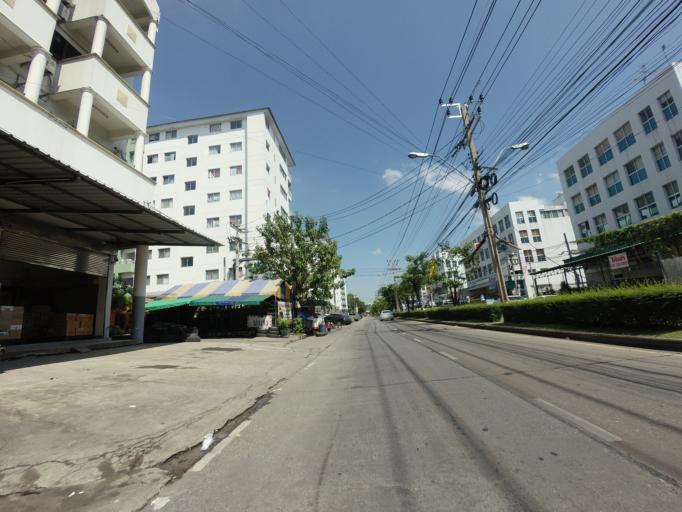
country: TH
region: Bangkok
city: Bang Kapi
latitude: 13.7736
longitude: 100.6413
